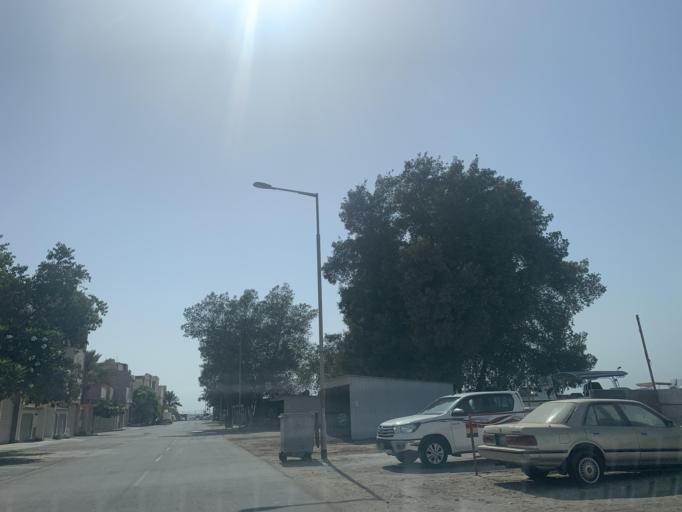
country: BH
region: Manama
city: Jidd Hafs
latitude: 26.2361
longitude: 50.5012
